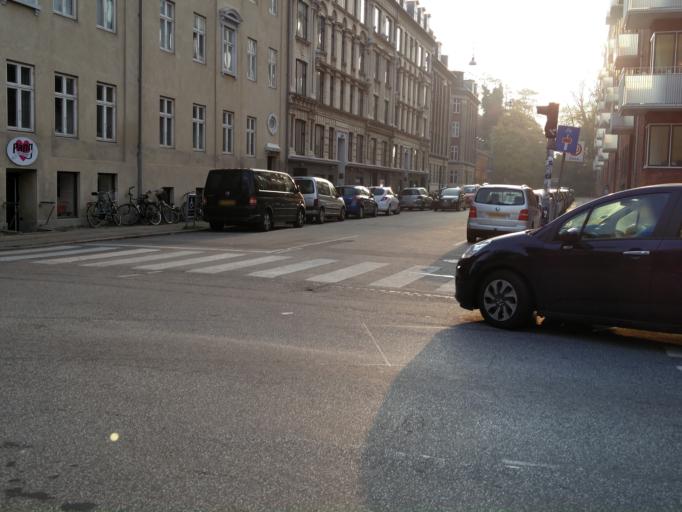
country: DK
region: Capital Region
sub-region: Kobenhavn
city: Christianshavn
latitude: 55.6724
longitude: 12.5942
